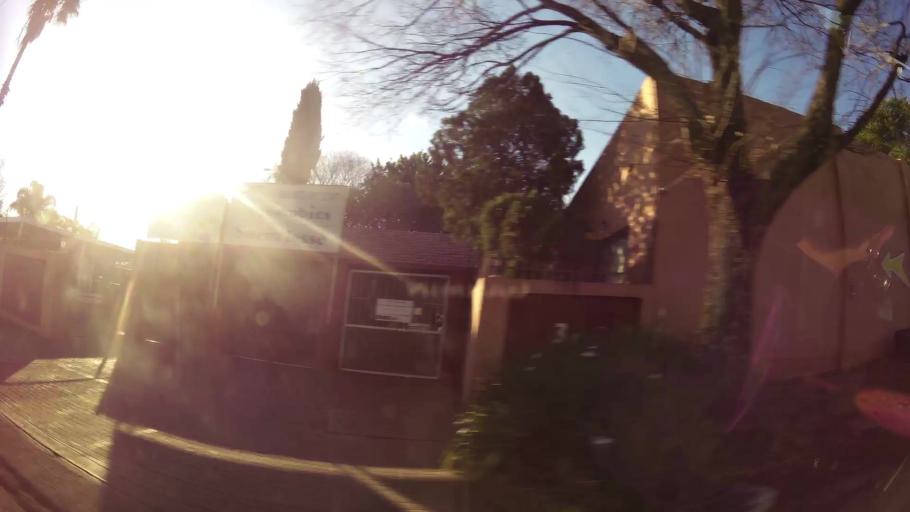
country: ZA
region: Gauteng
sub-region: City of Tshwane Metropolitan Municipality
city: Centurion
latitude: -25.8686
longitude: 28.1456
